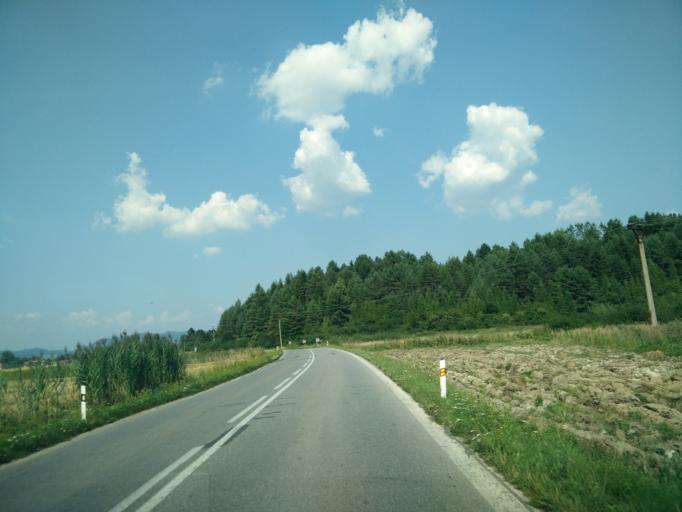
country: SK
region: Zilinsky
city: Rajec
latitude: 49.0589
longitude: 18.6259
